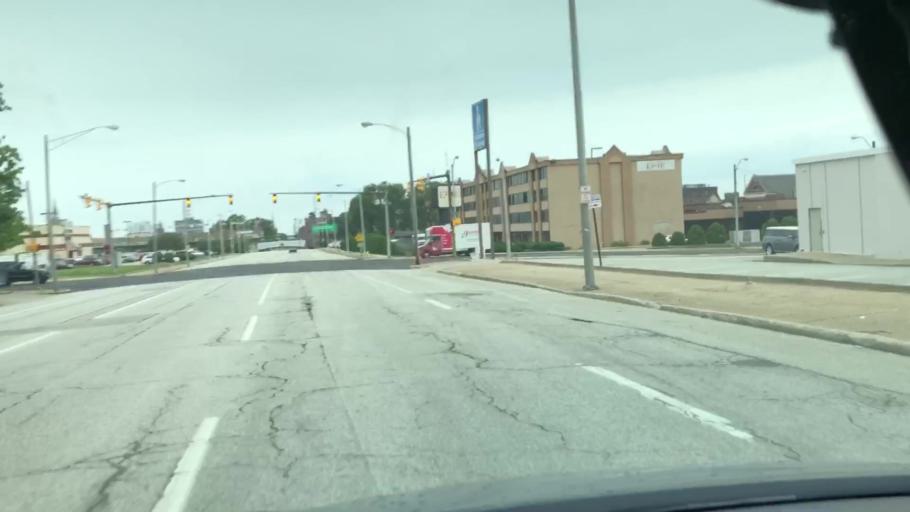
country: US
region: Pennsylvania
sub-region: Erie County
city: Erie
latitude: 42.1174
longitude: -80.0789
